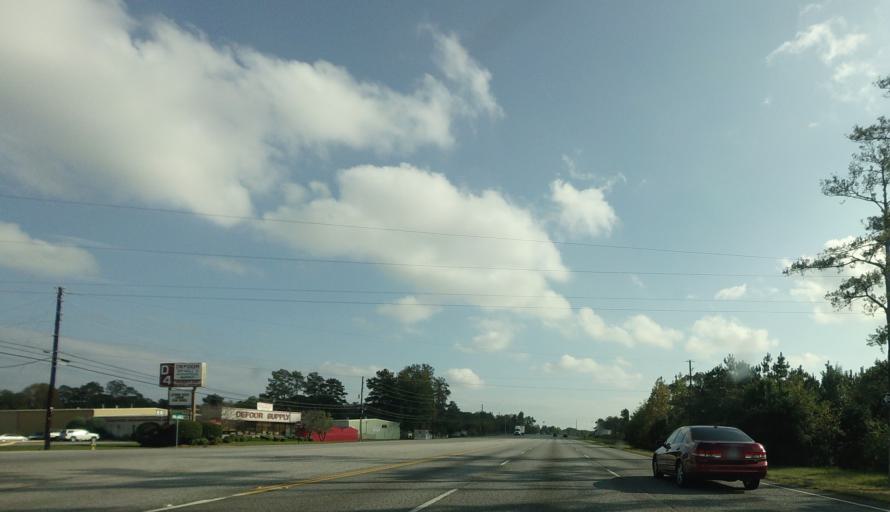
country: US
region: Georgia
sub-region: Bibb County
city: Macon
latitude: 32.7521
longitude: -83.6587
